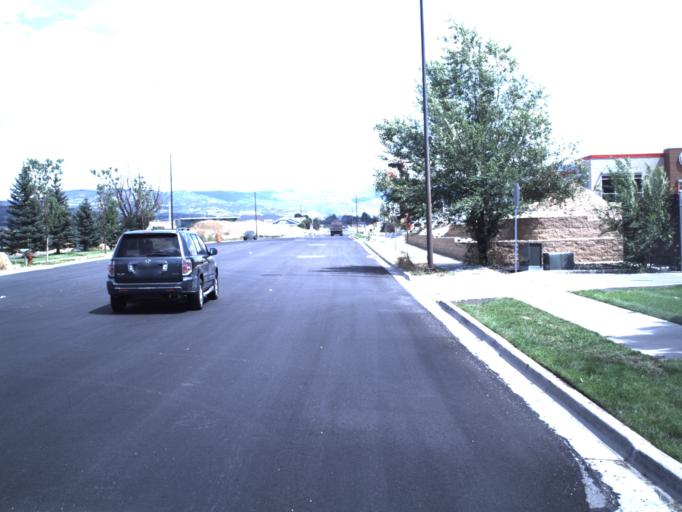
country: US
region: Utah
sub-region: Wasatch County
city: Heber
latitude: 40.4928
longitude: -111.4121
